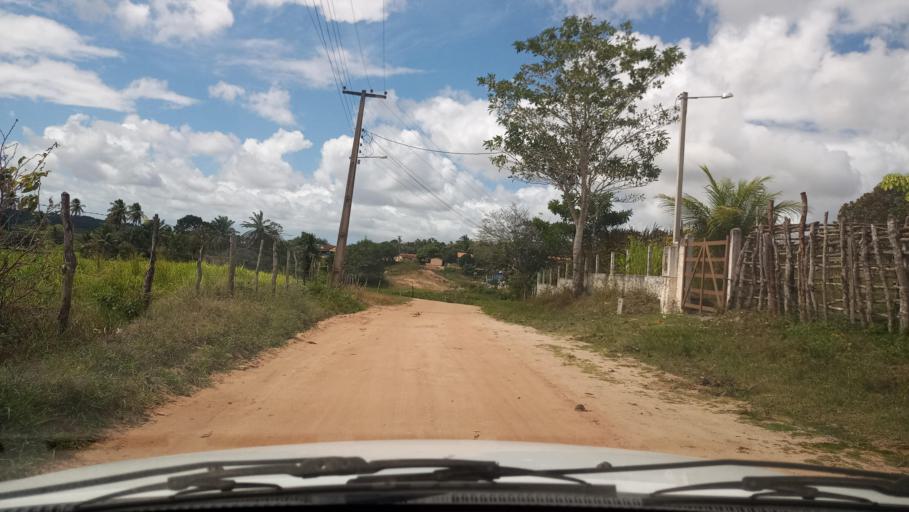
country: BR
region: Rio Grande do Norte
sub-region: Goianinha
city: Goianinha
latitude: -6.2617
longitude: -35.2587
